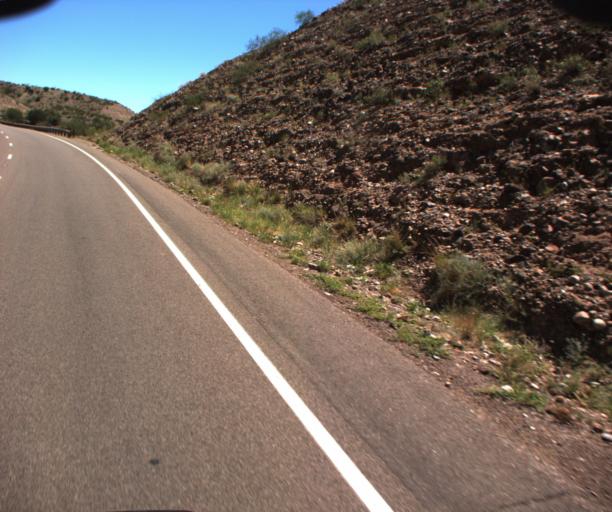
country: US
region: Arizona
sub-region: Greenlee County
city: Clifton
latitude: 33.0202
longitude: -109.2903
